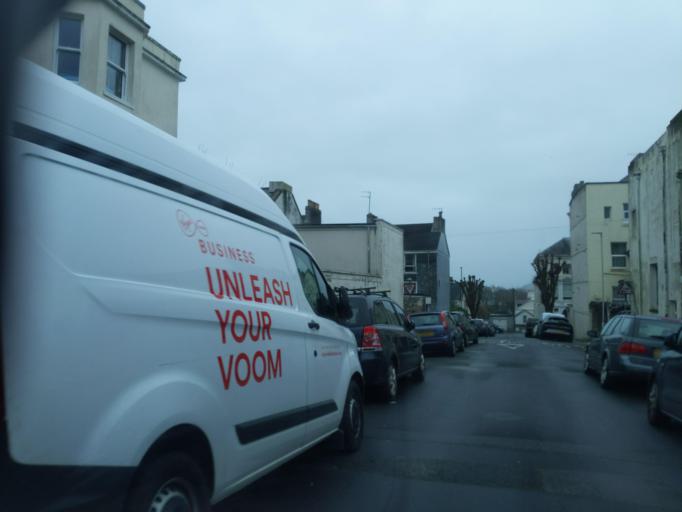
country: GB
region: England
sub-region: Cornwall
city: Millbrook
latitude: 50.3801
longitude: -4.1683
